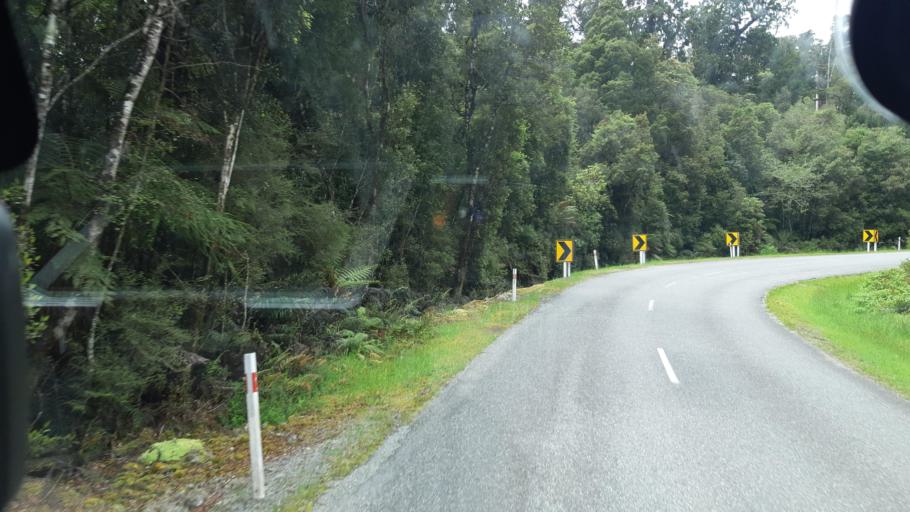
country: NZ
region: West Coast
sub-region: Westland District
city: Hokitika
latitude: -42.7748
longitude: 171.0924
